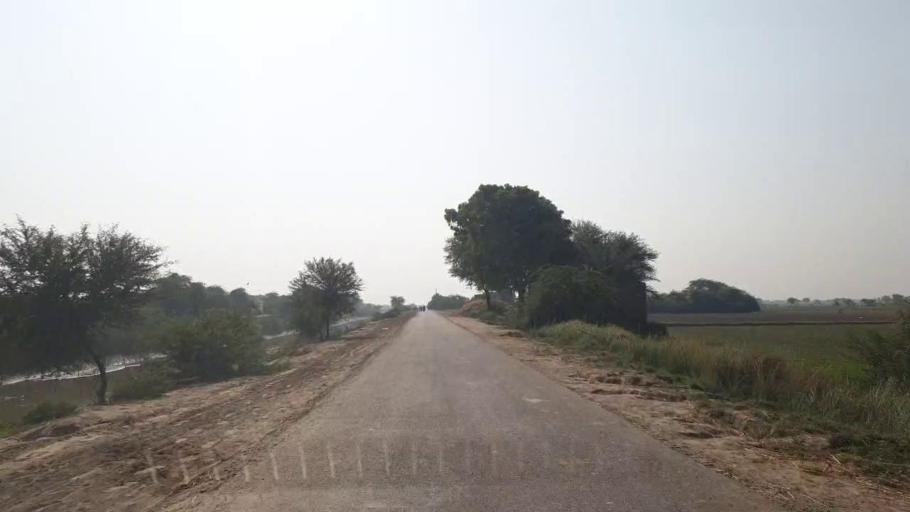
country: PK
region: Sindh
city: Matli
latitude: 24.9687
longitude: 68.5991
